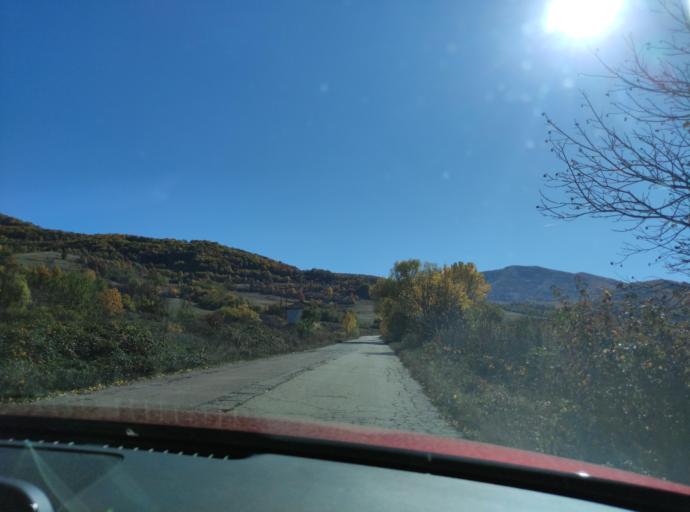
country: BG
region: Montana
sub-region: Obshtina Chiprovtsi
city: Chiprovtsi
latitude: 43.3895
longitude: 22.9220
